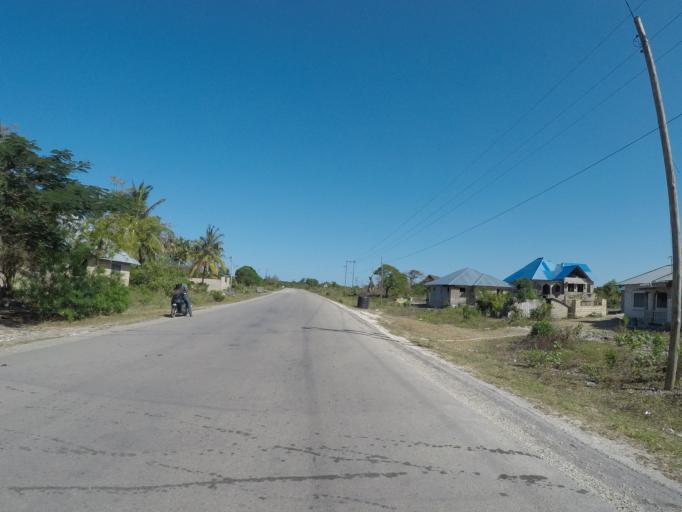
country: TZ
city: Kiwengwa
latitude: -6.1524
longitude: 39.5168
